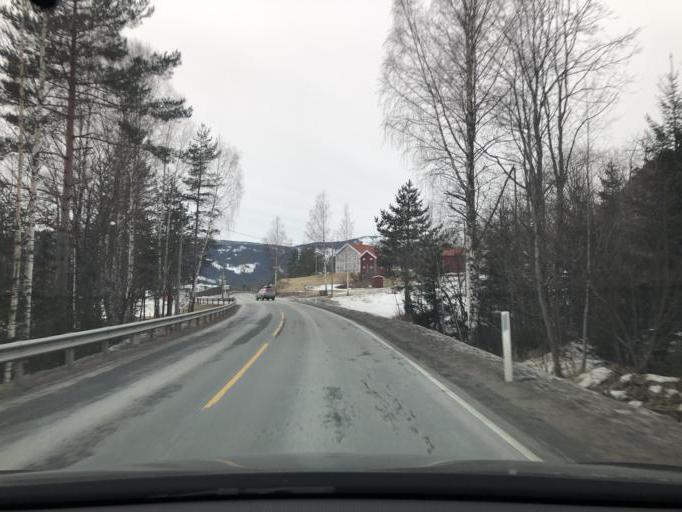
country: NO
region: Buskerud
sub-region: Ringerike
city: Honefoss
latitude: 60.4408
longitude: 10.0916
